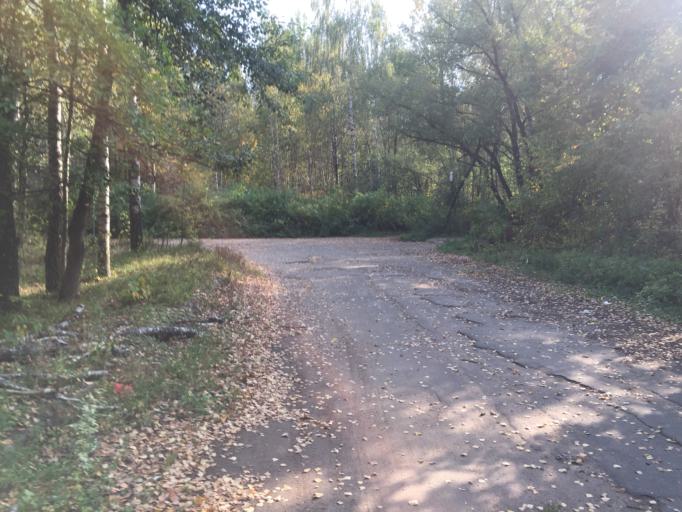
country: RU
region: Moscow
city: Babushkin
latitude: 55.8469
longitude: 37.7197
